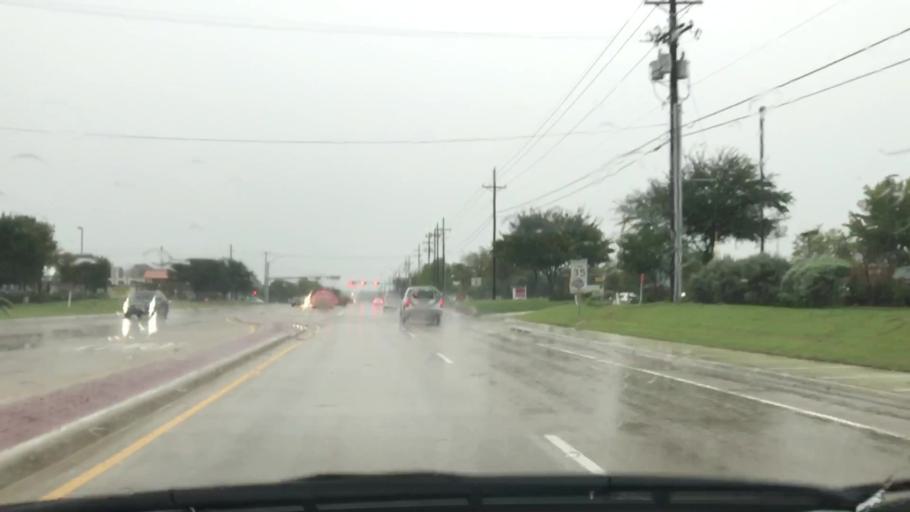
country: US
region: Texas
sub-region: Rockwall County
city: Rockwall
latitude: 32.8907
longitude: -96.4701
